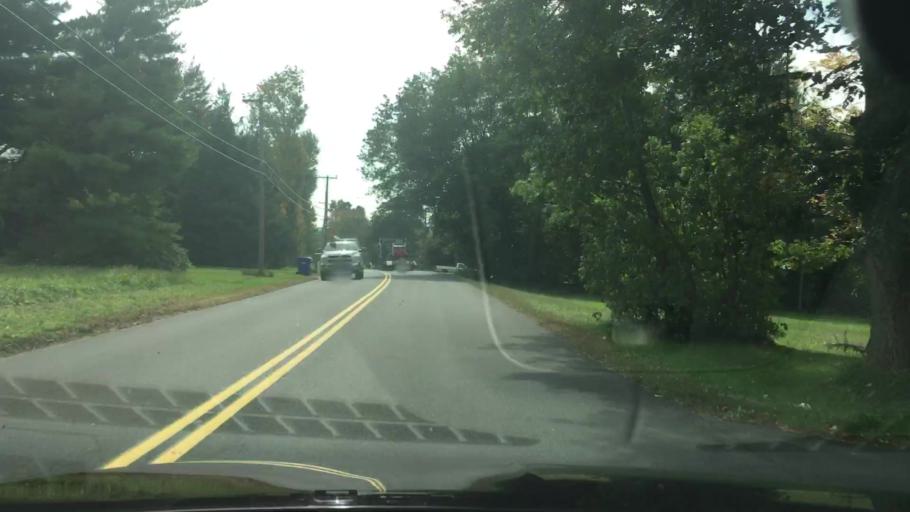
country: US
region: Connecticut
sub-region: Tolland County
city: Ellington
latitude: 41.9275
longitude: -72.4777
